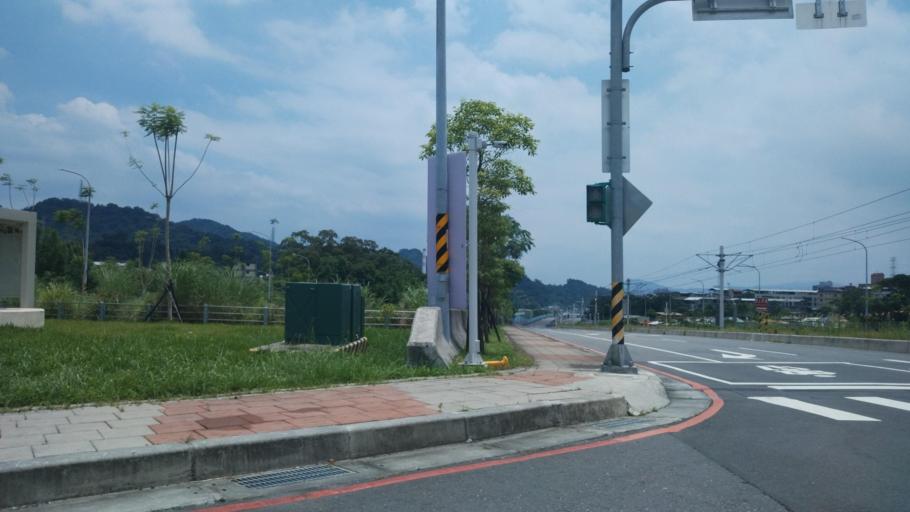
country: TW
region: Taipei
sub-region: Taipei
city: Banqiao
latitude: 24.9467
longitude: 121.4899
